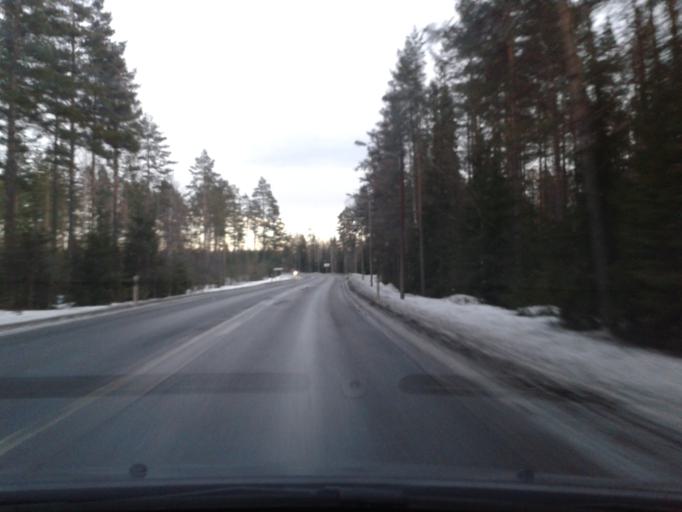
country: SE
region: Vaesternorrland
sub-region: Solleftea Kommun
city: Solleftea
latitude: 63.1542
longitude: 17.3293
